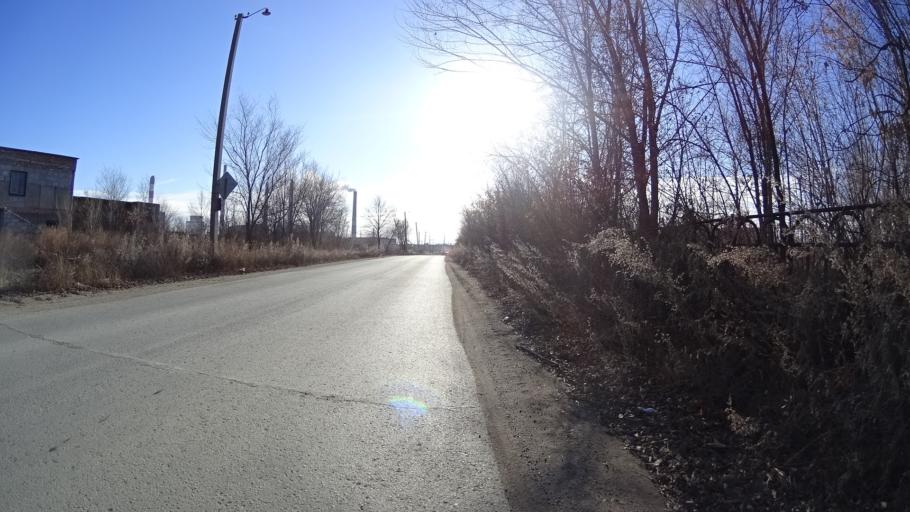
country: RU
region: Chelyabinsk
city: Troitsk
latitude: 54.0466
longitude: 61.6400
